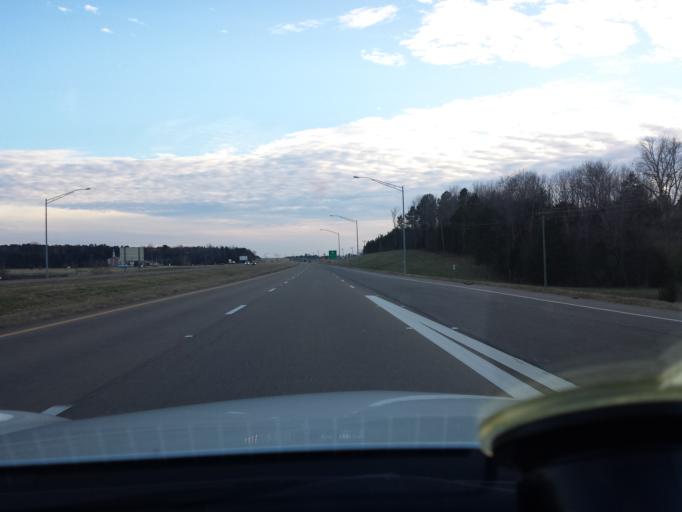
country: US
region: Mississippi
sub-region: Oktibbeha County
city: Starkville
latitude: 33.4571
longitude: -88.8536
